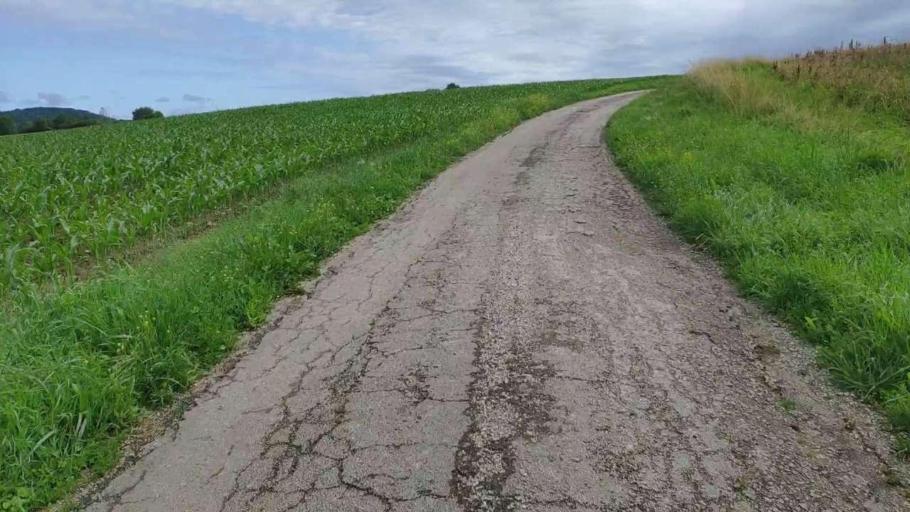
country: FR
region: Franche-Comte
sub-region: Departement du Jura
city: Poligny
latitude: 46.8058
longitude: 5.6050
